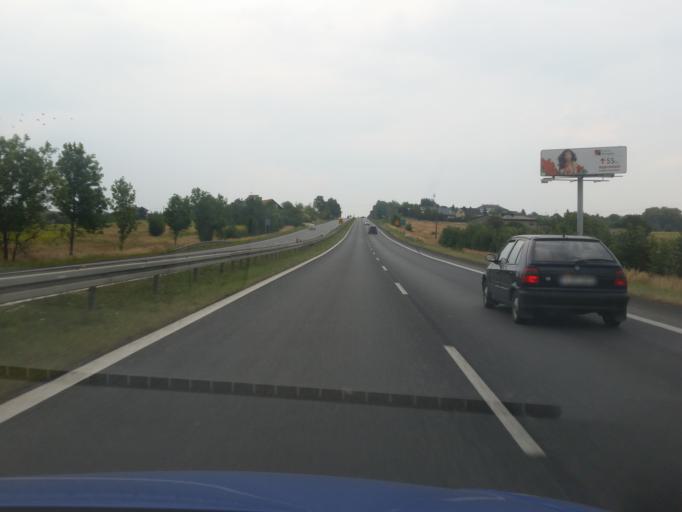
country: PL
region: Silesian Voivodeship
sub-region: Powiat bedzinski
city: Sarnow
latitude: 50.3671
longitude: 19.1370
